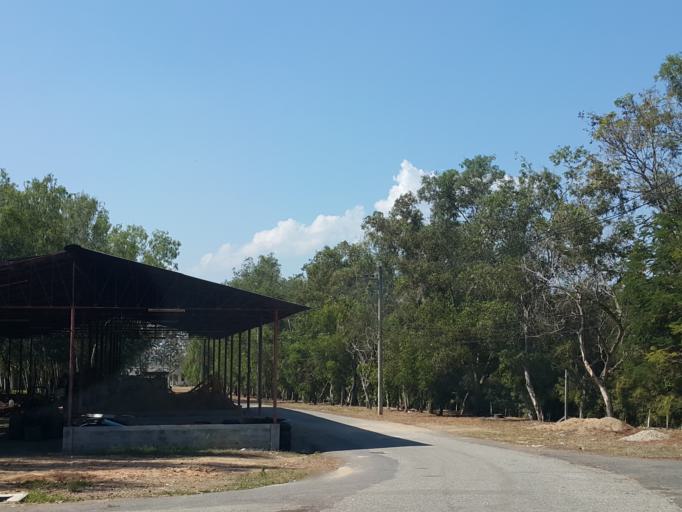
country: TH
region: Chiang Mai
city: Mae Taeng
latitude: 19.0319
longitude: 98.9882
